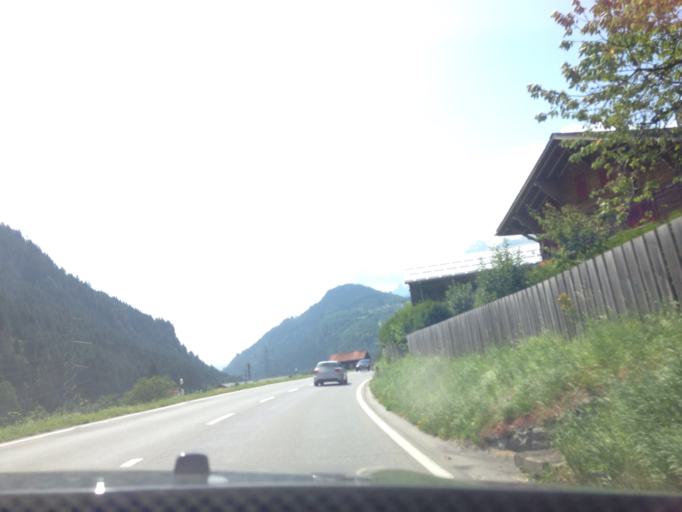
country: CH
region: Grisons
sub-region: Surselva District
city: Ilanz
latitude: 46.7756
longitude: 9.1496
